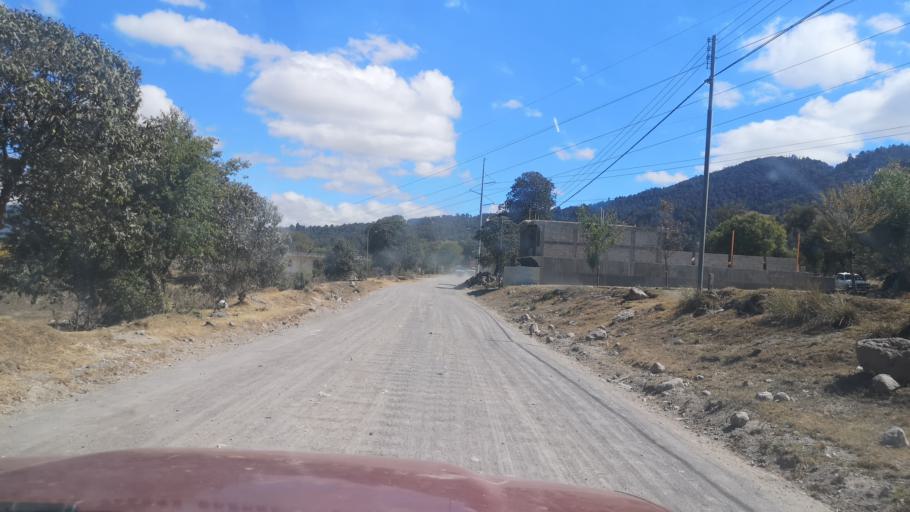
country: GT
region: Quetzaltenango
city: Quetzaltenango
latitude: 14.8022
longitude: -91.5378
